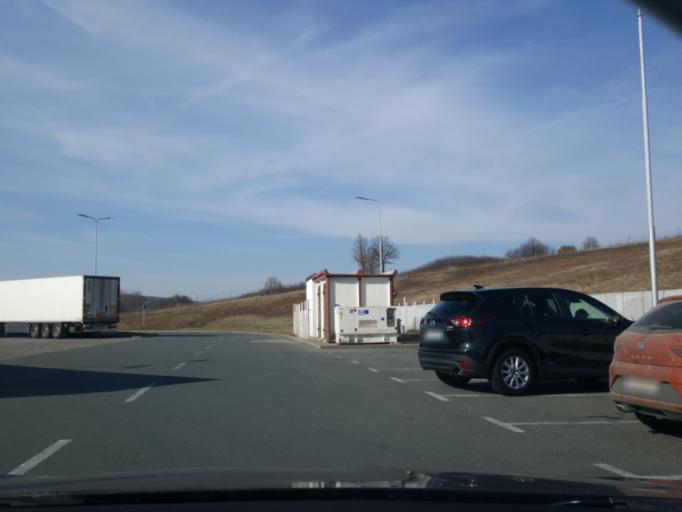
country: RS
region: Central Serbia
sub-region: Nisavski Okrug
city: Razanj
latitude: 43.6419
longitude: 21.5576
